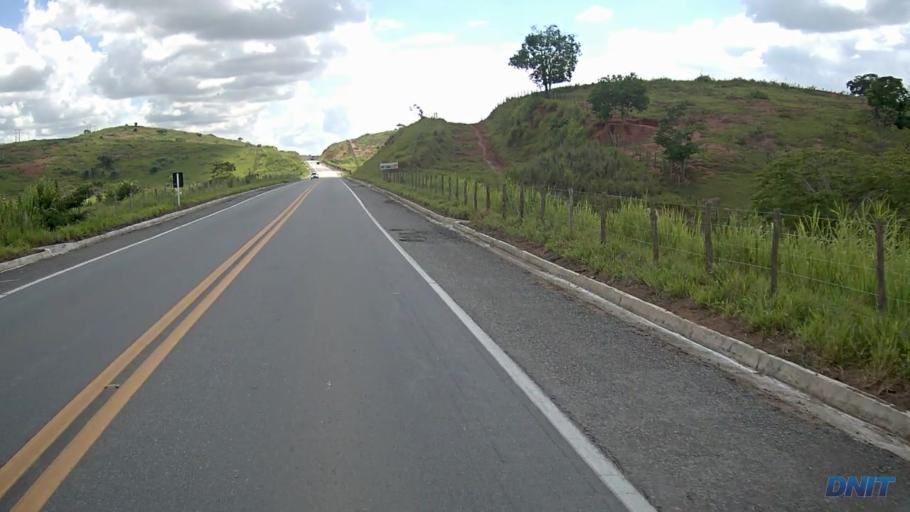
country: BR
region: Minas Gerais
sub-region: Governador Valadares
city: Governador Valadares
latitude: -18.9947
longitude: -42.1189
